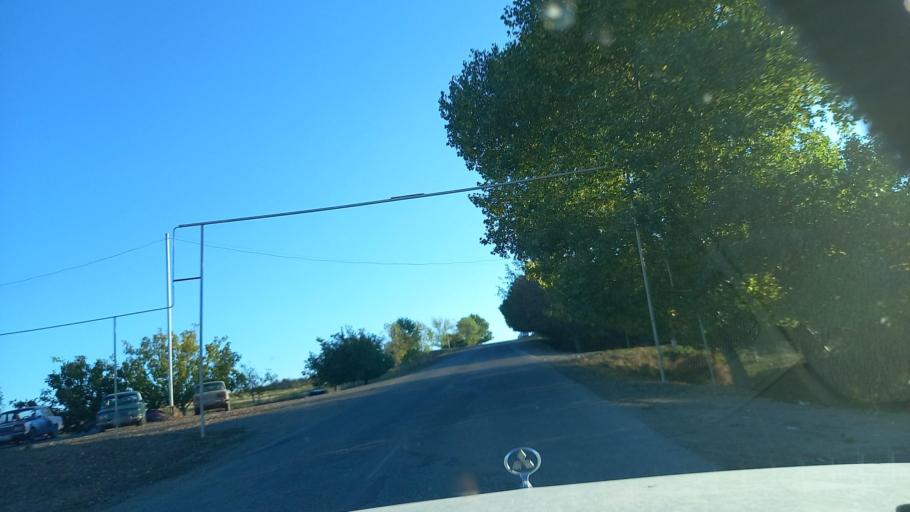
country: AZ
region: Shamkir Rayon
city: Shamkhor
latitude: 40.7725
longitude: 45.9584
